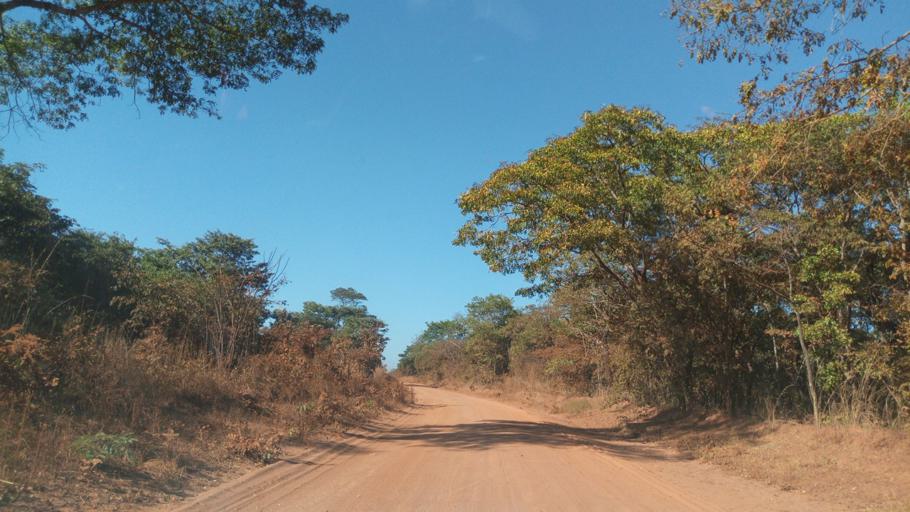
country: ZM
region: Luapula
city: Mwense
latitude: -10.6360
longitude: 28.4092
